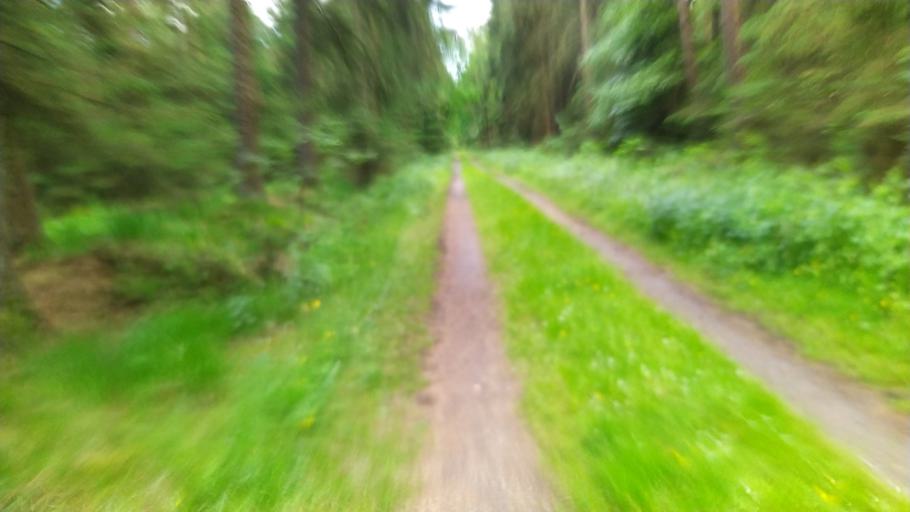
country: DE
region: Lower Saxony
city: Deinstedt
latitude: 53.4410
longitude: 9.2468
